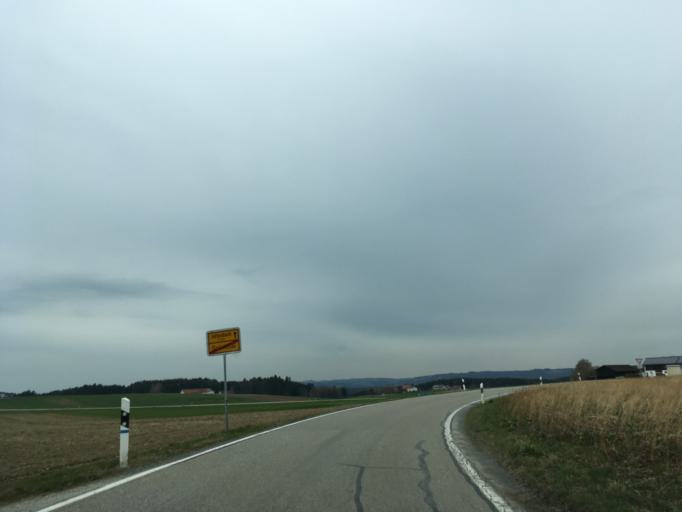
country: DE
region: Bavaria
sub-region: Upper Bavaria
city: Jettenbach
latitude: 48.1416
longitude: 12.3935
